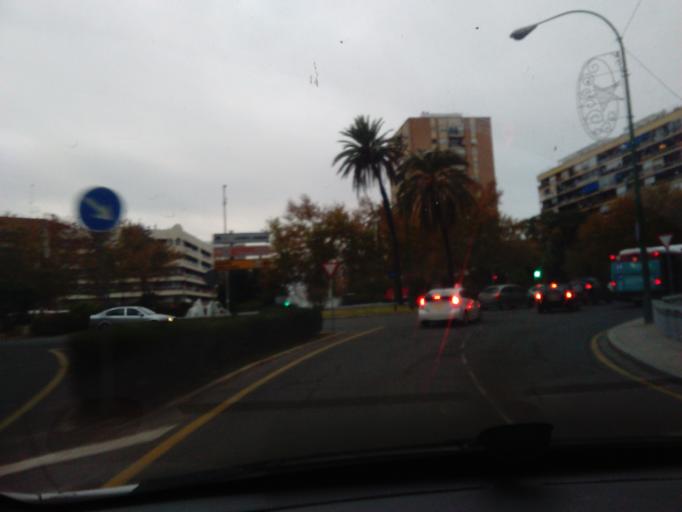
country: ES
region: Andalusia
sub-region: Provincia de Sevilla
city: Sevilla
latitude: 37.3815
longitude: -5.9651
